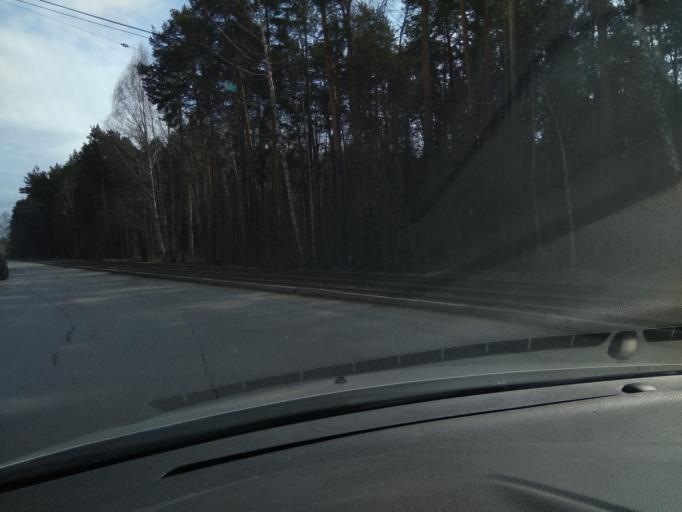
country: RU
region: Sverdlovsk
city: Shuvakish
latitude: 56.8835
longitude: 60.4988
